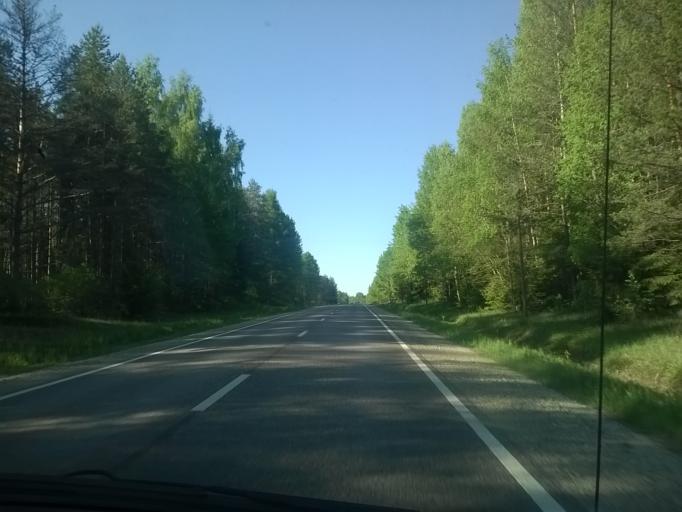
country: LV
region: Valkas Rajons
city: Valka
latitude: 57.7322
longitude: 25.9413
